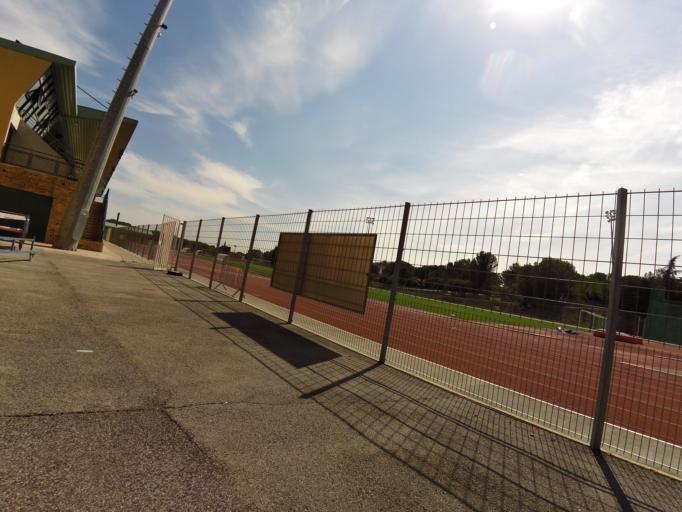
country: FR
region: Languedoc-Roussillon
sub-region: Departement du Gard
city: Vergeze
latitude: 43.7506
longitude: 4.2189
